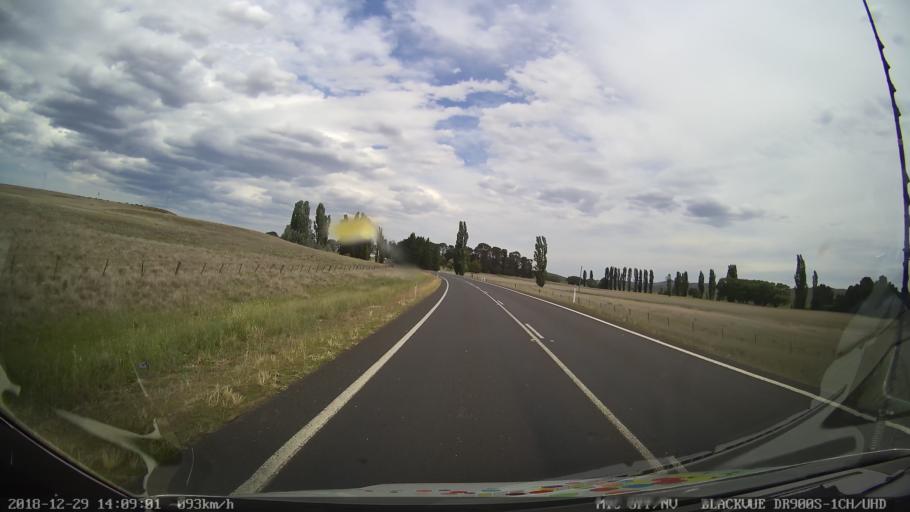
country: AU
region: New South Wales
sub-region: Cooma-Monaro
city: Cooma
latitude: -36.3731
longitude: 149.2122
